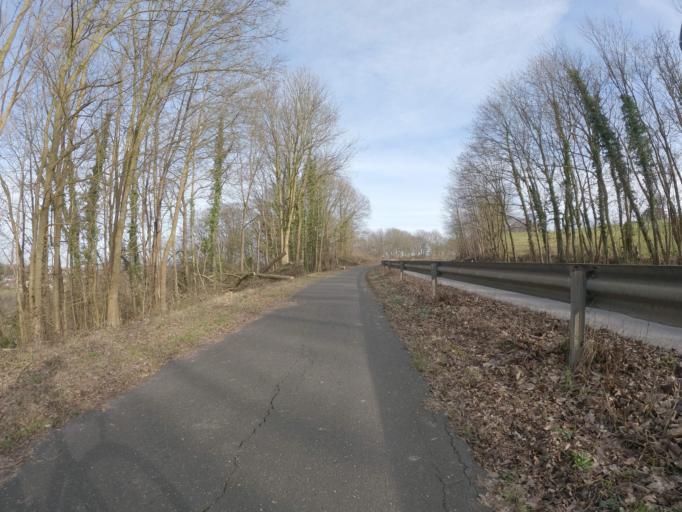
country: DE
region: North Rhine-Westphalia
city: Stolberg
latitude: 50.7610
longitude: 6.2086
